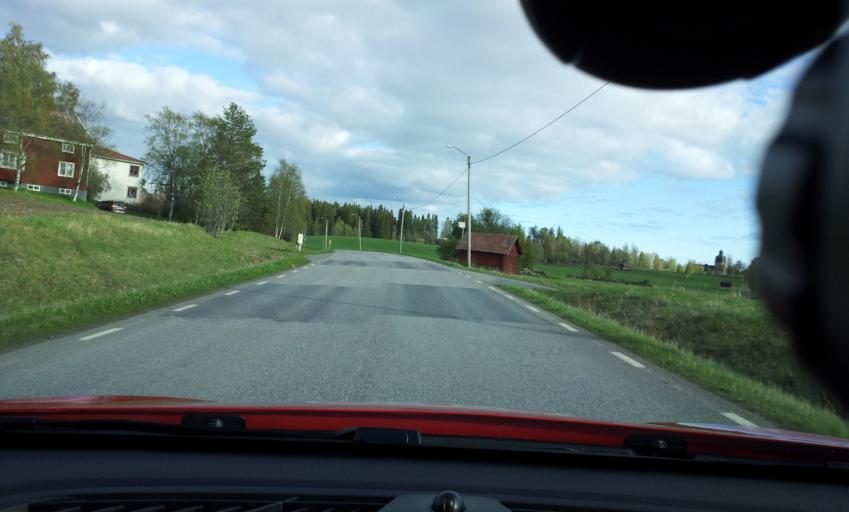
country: SE
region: Jaemtland
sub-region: Krokoms Kommun
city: Krokom
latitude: 63.2541
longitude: 14.4103
